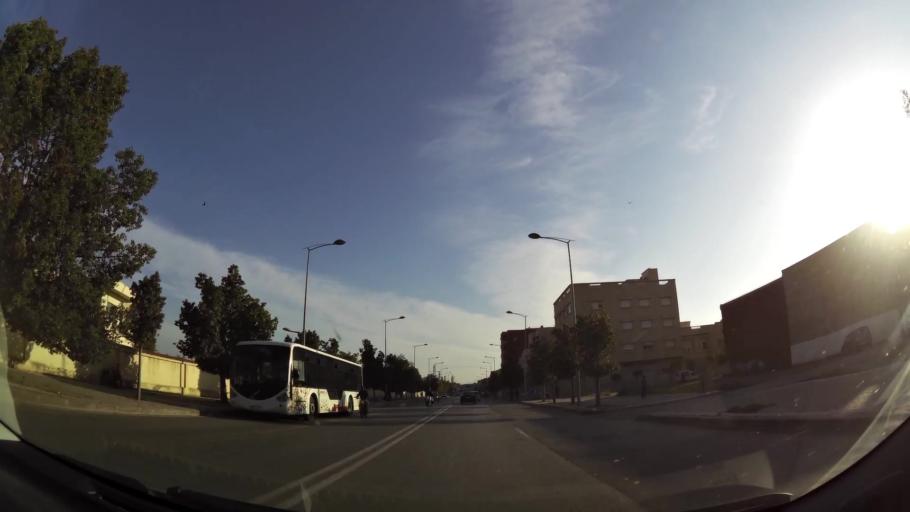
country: MA
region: Oriental
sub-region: Oujda-Angad
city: Oujda
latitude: 34.7068
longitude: -1.8931
